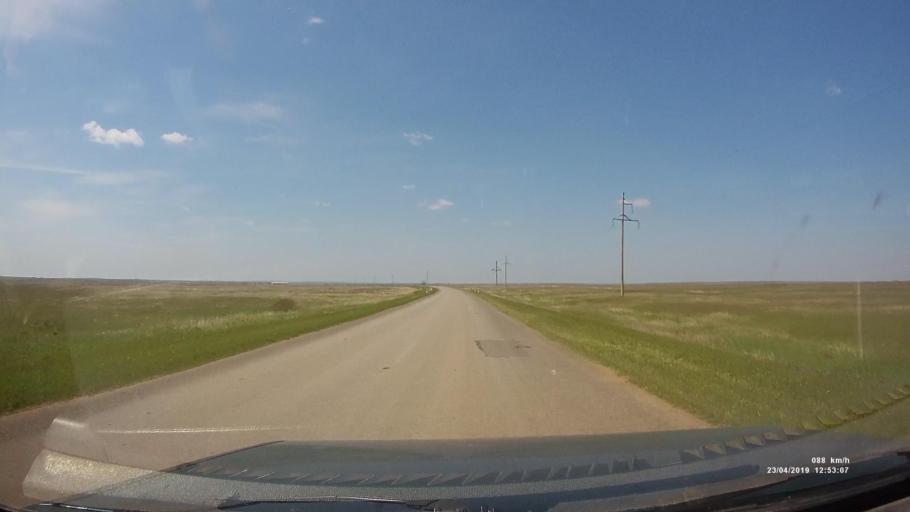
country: RU
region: Kalmykiya
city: Yashalta
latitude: 46.5712
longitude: 42.6005
